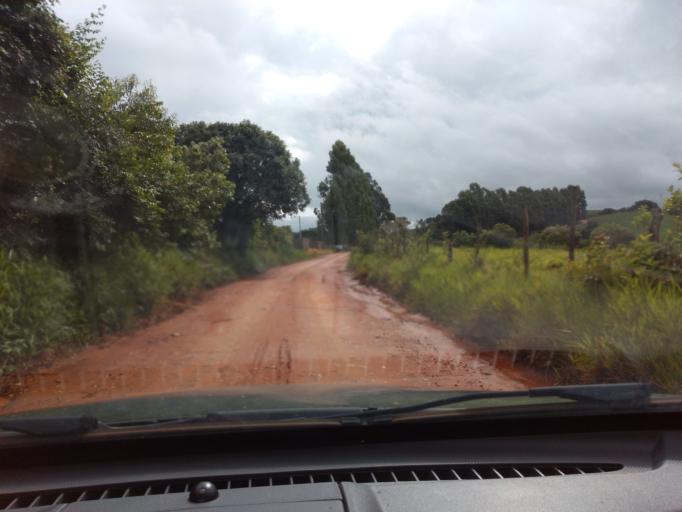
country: BR
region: Minas Gerais
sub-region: Lavras
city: Lavras
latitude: -21.5076
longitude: -44.9201
